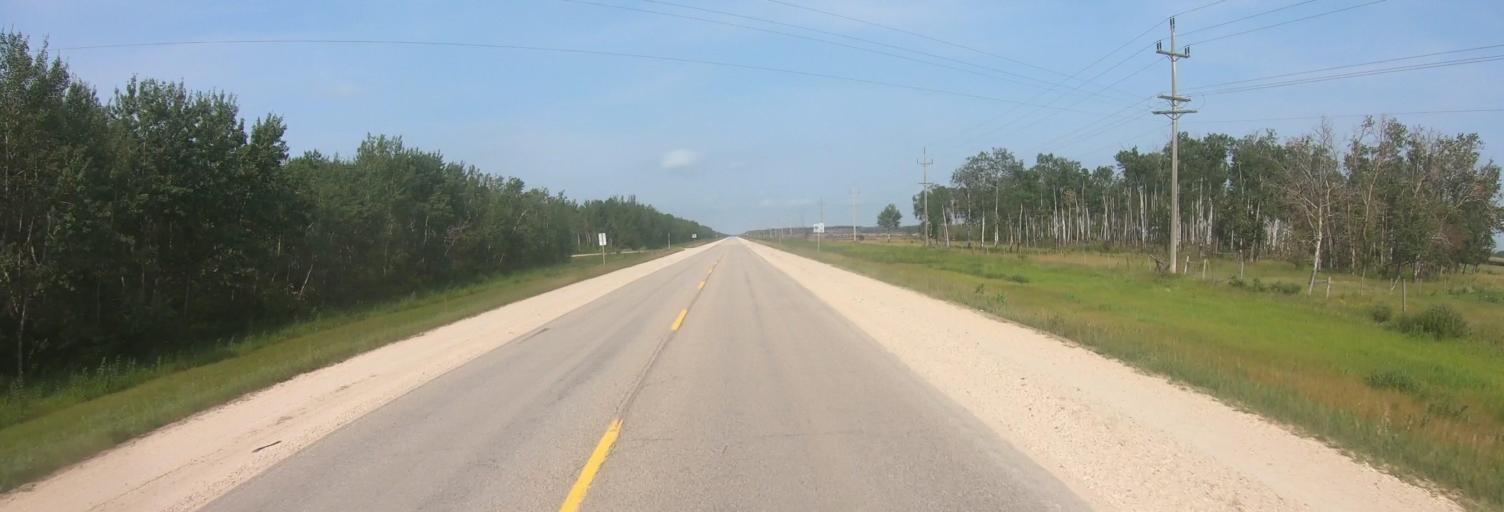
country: CA
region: Manitoba
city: La Broquerie
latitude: 49.3264
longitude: -96.5998
